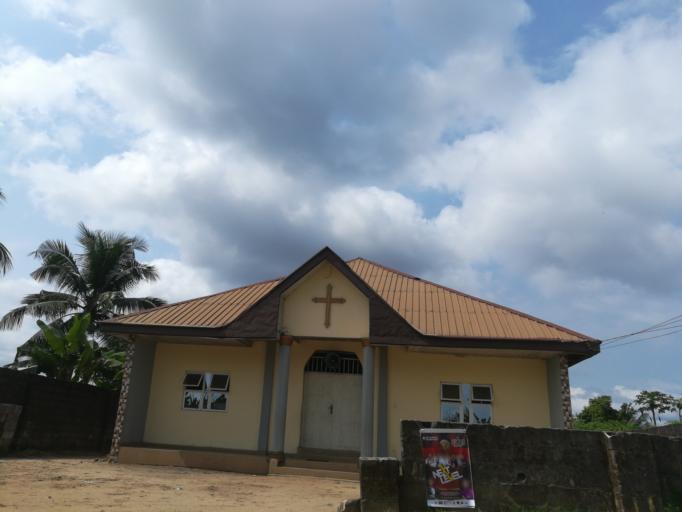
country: NG
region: Rivers
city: Okrika
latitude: 4.7440
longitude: 7.1138
